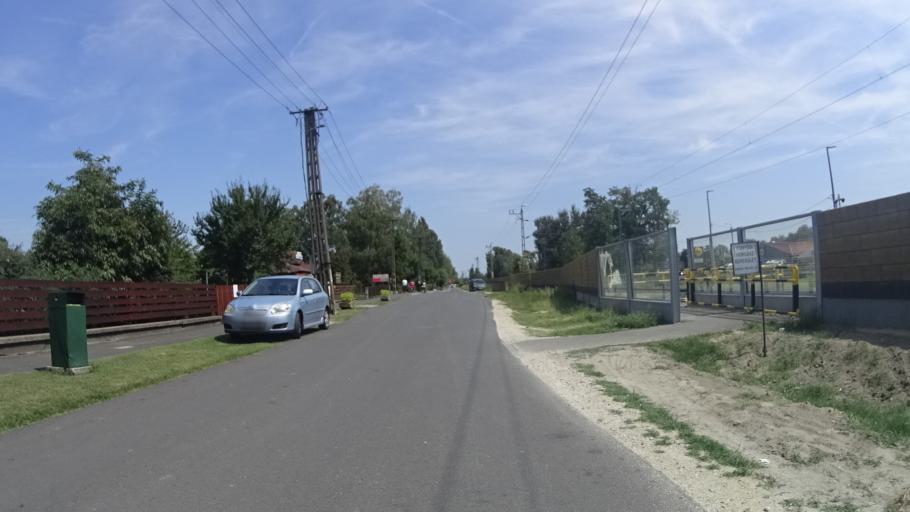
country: HU
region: Somogy
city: Fonyod
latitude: 46.7524
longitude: 17.5670
